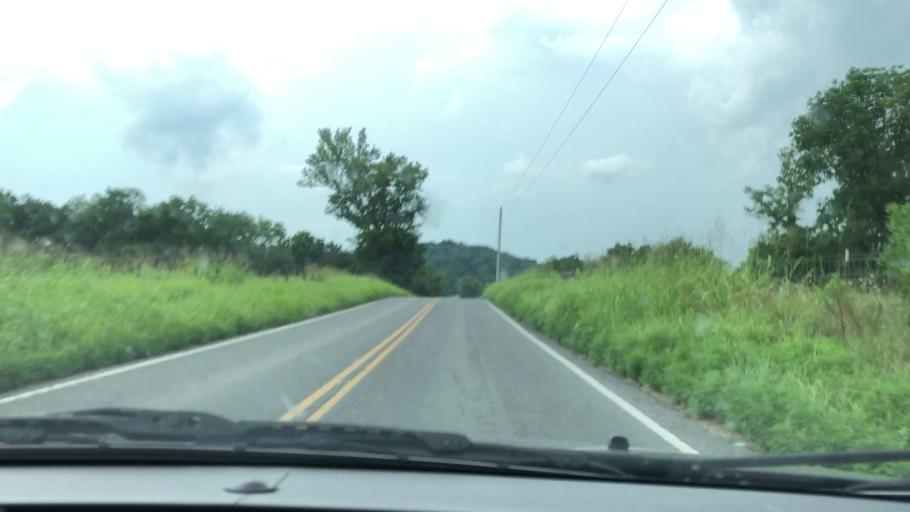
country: US
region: Tennessee
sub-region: Maury County
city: Spring Hill
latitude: 35.7862
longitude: -87.0041
